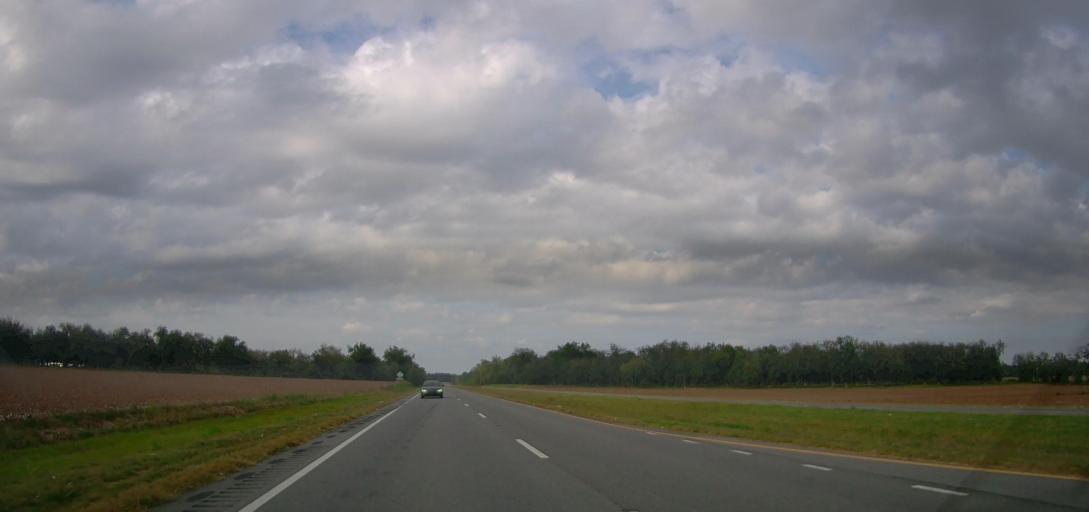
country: US
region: Georgia
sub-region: Thomas County
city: Meigs
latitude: 31.0326
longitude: -84.0636
